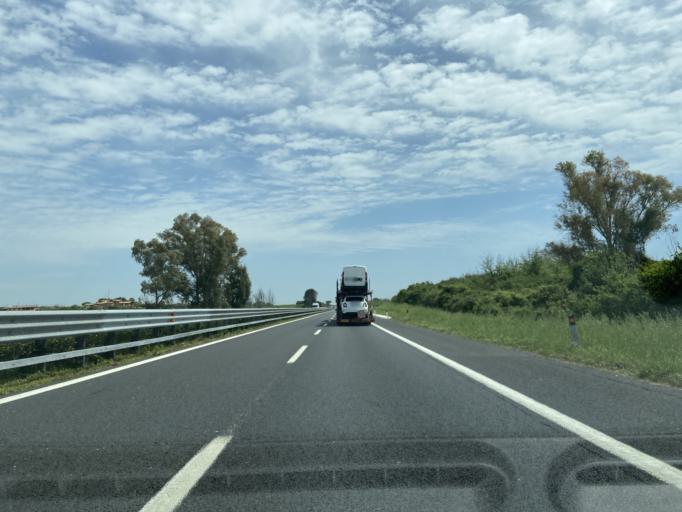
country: IT
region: Latium
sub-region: Citta metropolitana di Roma Capitale
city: Marina di Cerveteri
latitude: 41.9949
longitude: 12.0532
